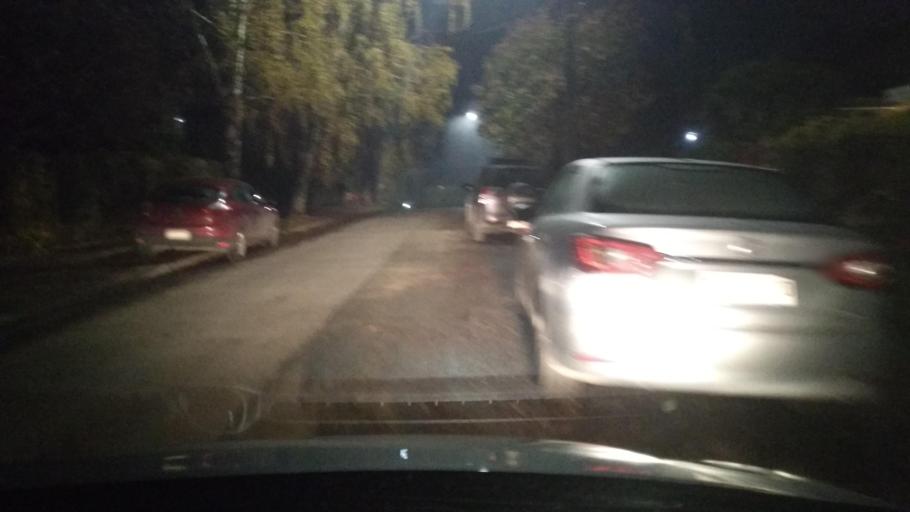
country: CL
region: Los Rios
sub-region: Provincia de Valdivia
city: Valdivia
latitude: -39.8156
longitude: -73.2582
